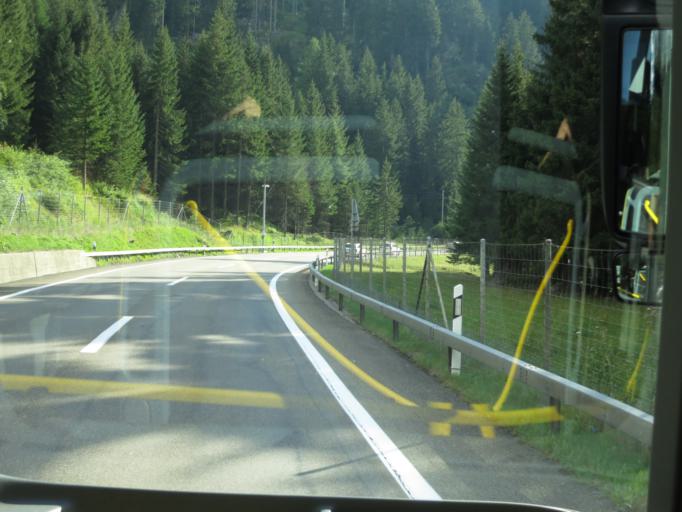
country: CH
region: Grisons
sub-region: Hinterrhein District
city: Thusis
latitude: 46.5665
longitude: 9.3870
